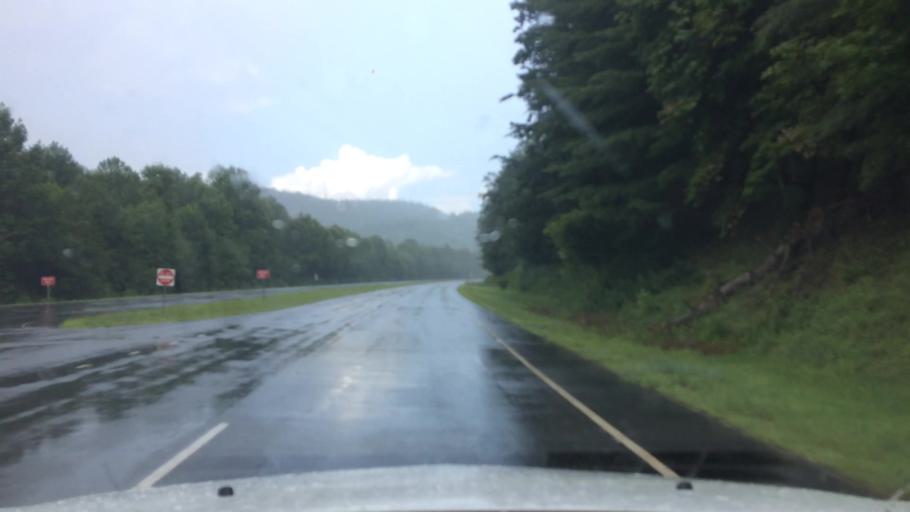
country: US
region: North Carolina
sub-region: Wilkes County
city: Millers Creek
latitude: 36.1944
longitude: -81.4218
